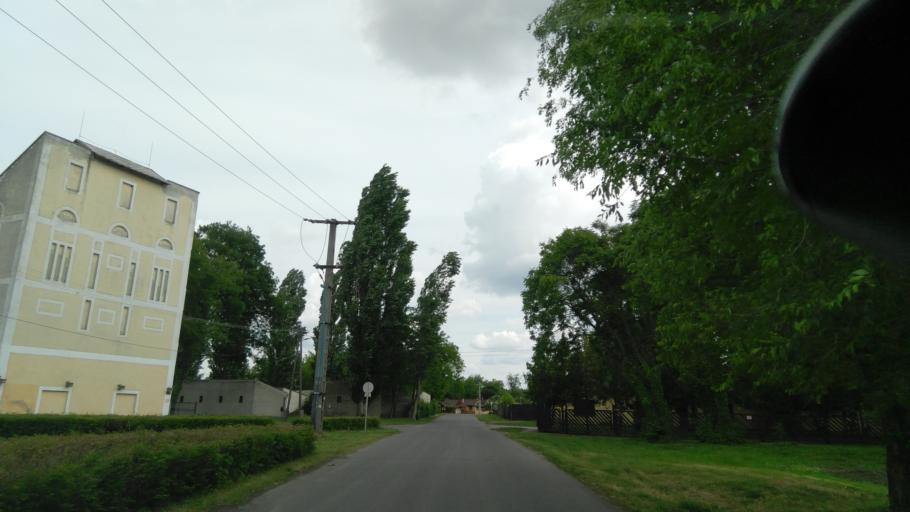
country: HU
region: Bekes
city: Mezohegyes
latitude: 46.3151
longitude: 20.8219
